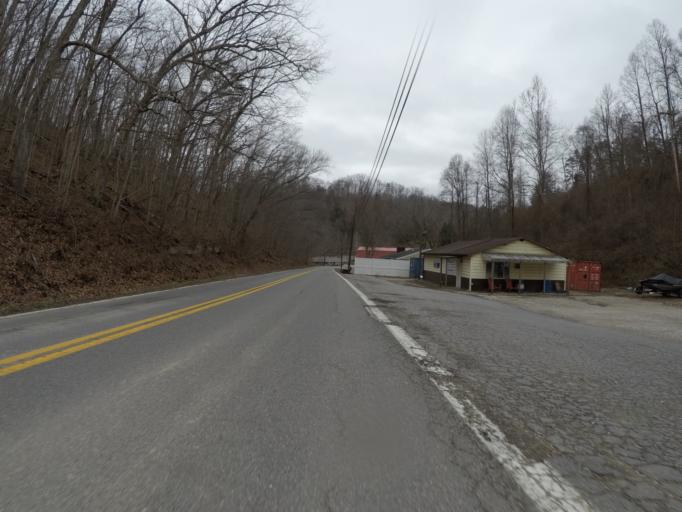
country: US
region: West Virginia
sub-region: Cabell County
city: Barboursville
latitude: 38.4404
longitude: -82.2929
